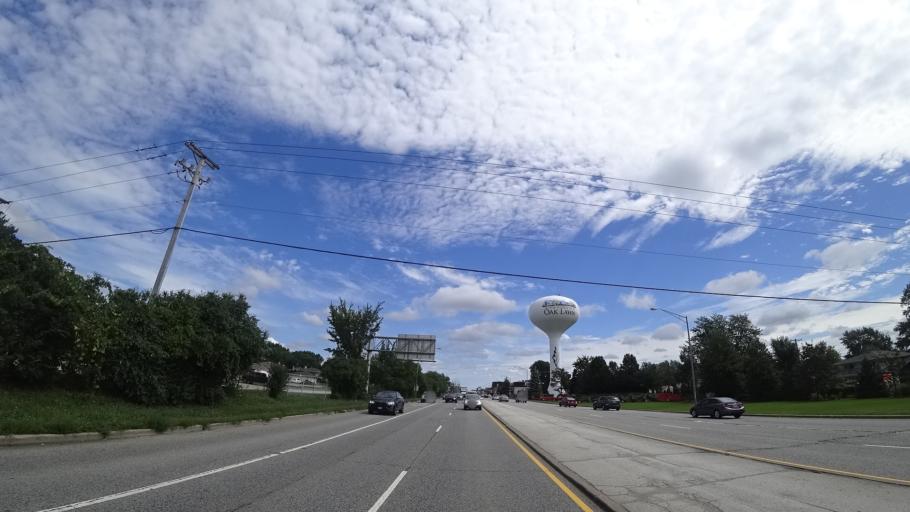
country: US
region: Illinois
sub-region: Cook County
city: Burbank
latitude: 41.7194
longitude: -87.7942
